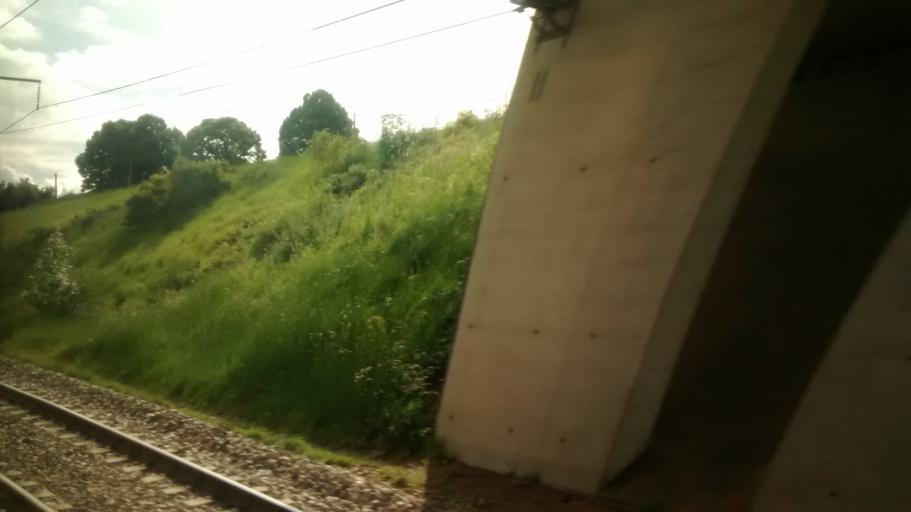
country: FR
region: Centre
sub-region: Departement d'Eure-et-Loir
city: Auneau
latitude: 48.4461
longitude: 1.7868
